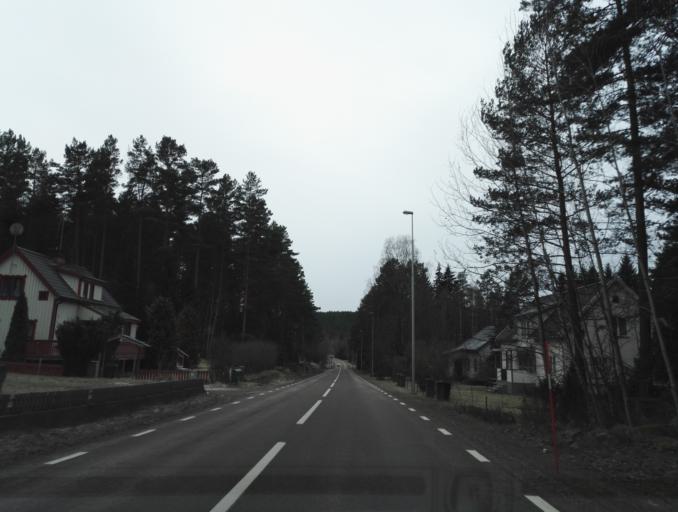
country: SE
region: Kalmar
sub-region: Hultsfreds Kommun
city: Virserum
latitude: 57.3338
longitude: 15.5911
